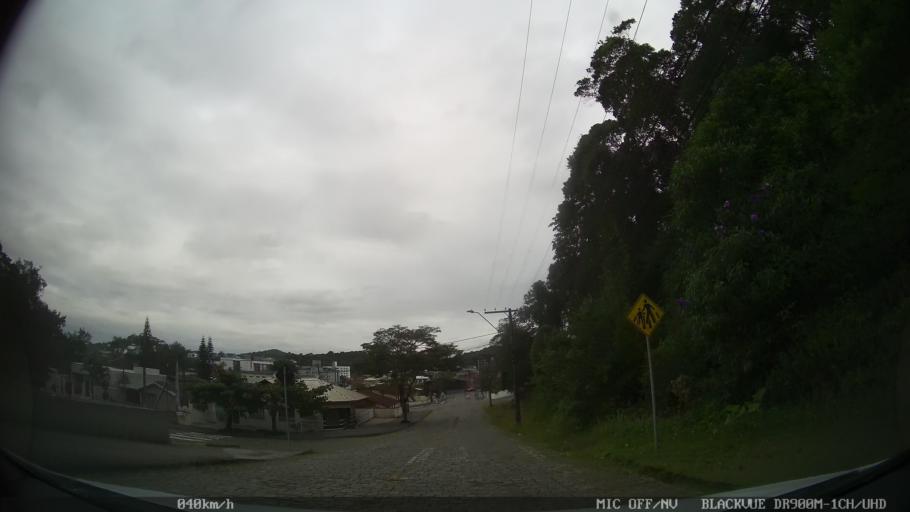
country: BR
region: Santa Catarina
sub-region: Joinville
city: Joinville
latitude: -26.2828
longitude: -48.8824
